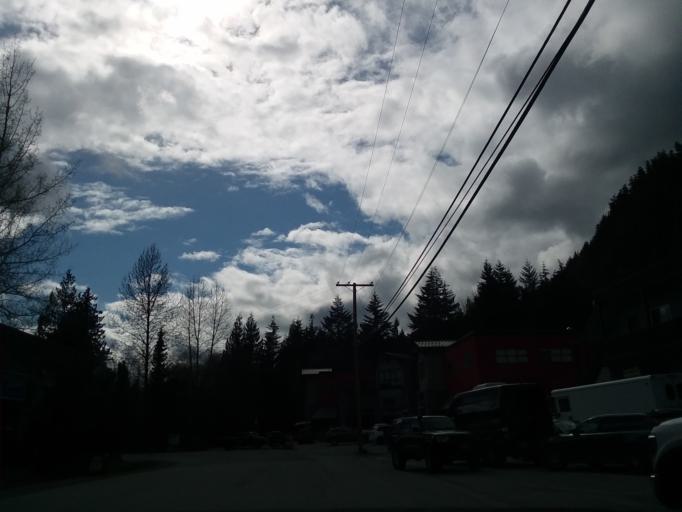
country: CA
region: British Columbia
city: Whistler
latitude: 50.0890
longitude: -123.0383
